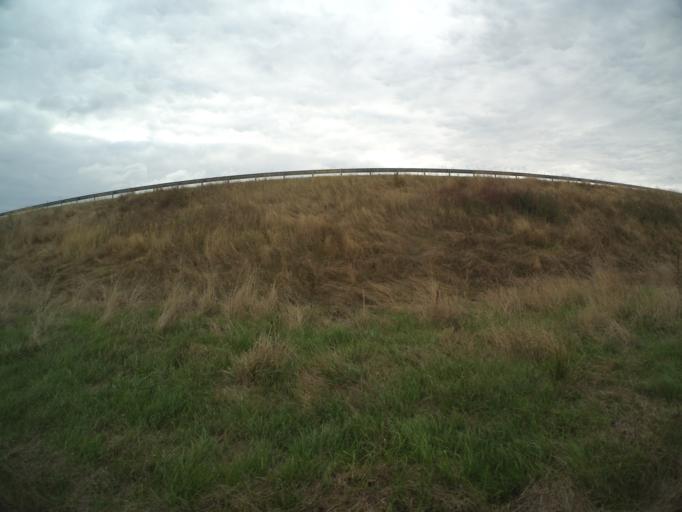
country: FR
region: Centre
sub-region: Departement d'Indre-et-Loire
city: Auzouer-en-Touraine
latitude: 47.4913
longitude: 0.9400
